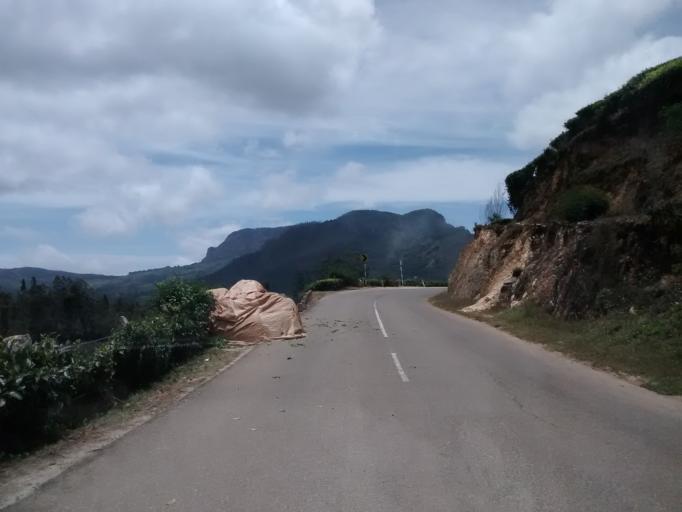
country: IN
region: Tamil Nadu
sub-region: Theni
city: Bodinayakkanur
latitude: 10.1308
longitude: 77.2307
